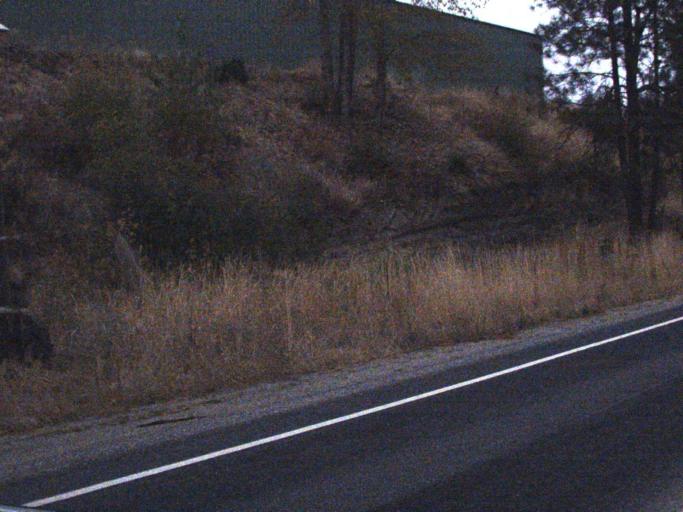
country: US
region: Washington
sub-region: Stevens County
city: Kettle Falls
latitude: 48.6606
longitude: -118.1136
